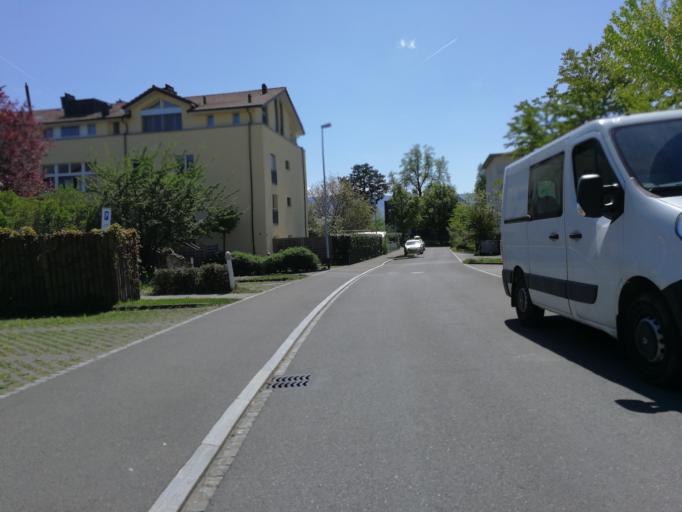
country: CH
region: Zurich
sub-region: Bezirk Meilen
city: Maennedorf / Dorfkern
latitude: 47.2601
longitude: 8.6855
